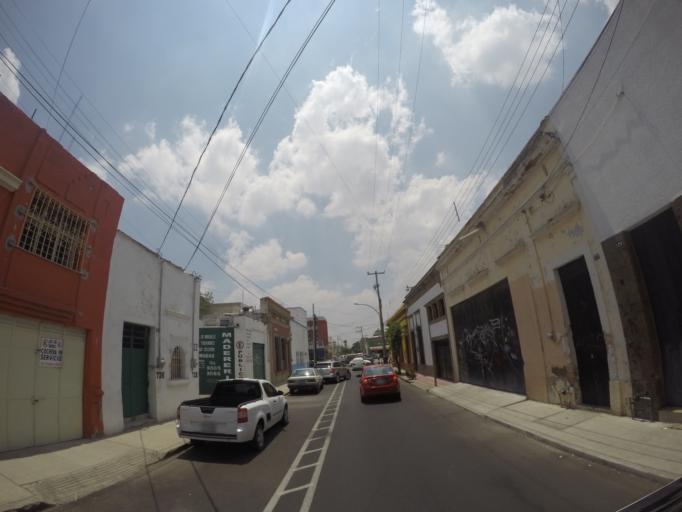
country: MX
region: Jalisco
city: Guadalajara
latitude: 20.6802
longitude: -103.3549
